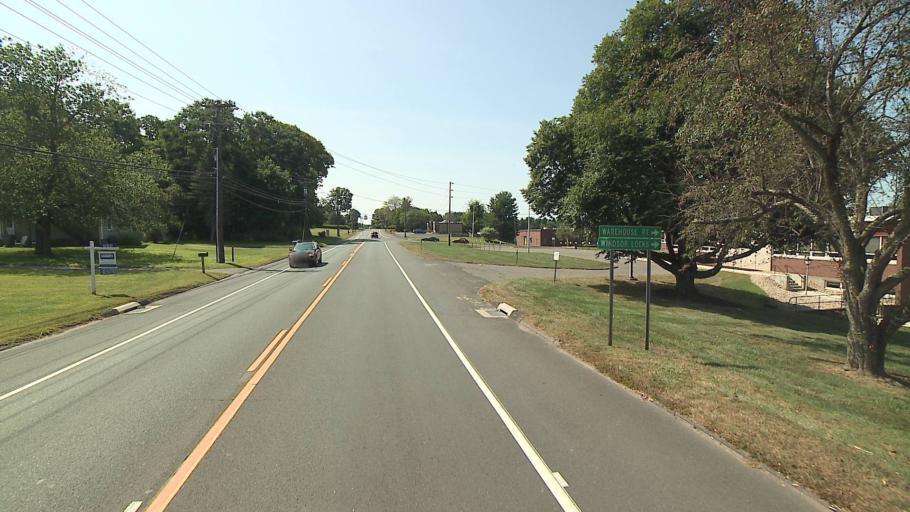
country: US
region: Connecticut
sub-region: Hartford County
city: Windsor Locks
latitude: 41.9438
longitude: -72.6028
